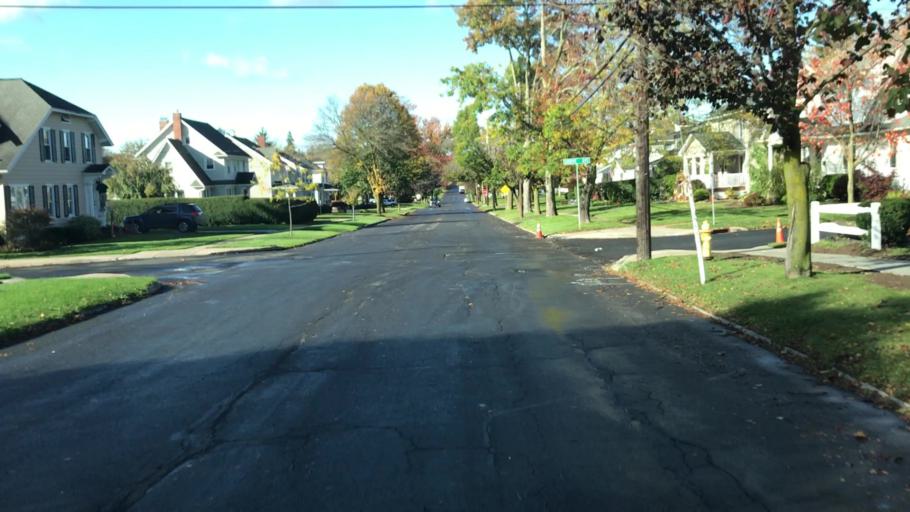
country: US
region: New York
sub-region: Cayuga County
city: Auburn
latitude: 42.9204
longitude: -76.5572
